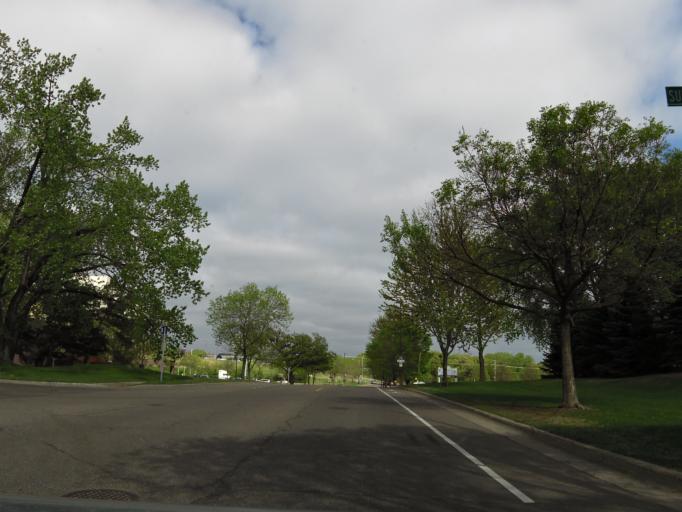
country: US
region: Minnesota
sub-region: Ramsey County
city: Maplewood
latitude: 44.9486
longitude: -93.0080
